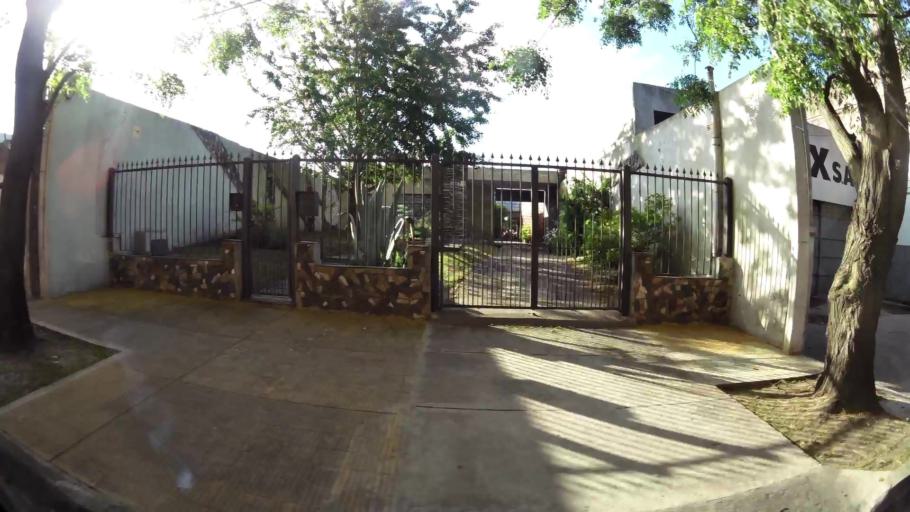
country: UY
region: Montevideo
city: Montevideo
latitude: -34.8712
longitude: -56.1365
